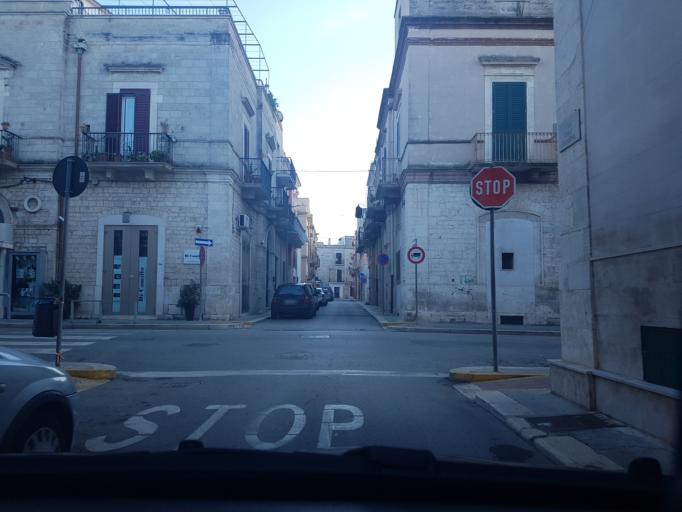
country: IT
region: Apulia
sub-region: Provincia di Bari
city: Bitritto
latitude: 41.0424
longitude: 16.8254
